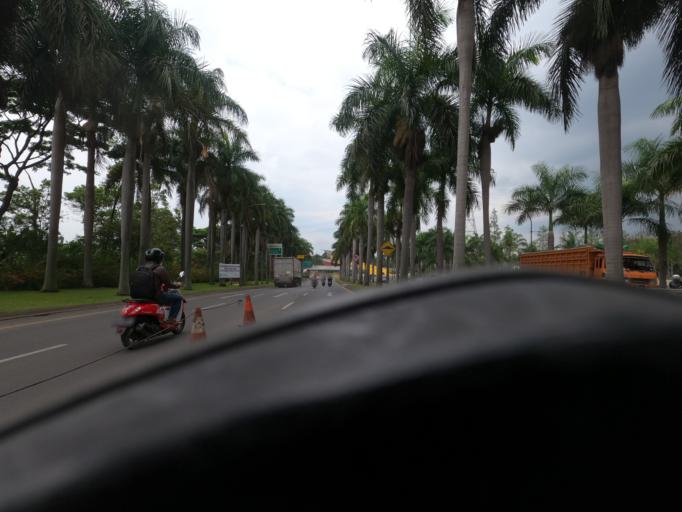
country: ID
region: West Java
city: Padalarang
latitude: -6.8508
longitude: 107.4951
